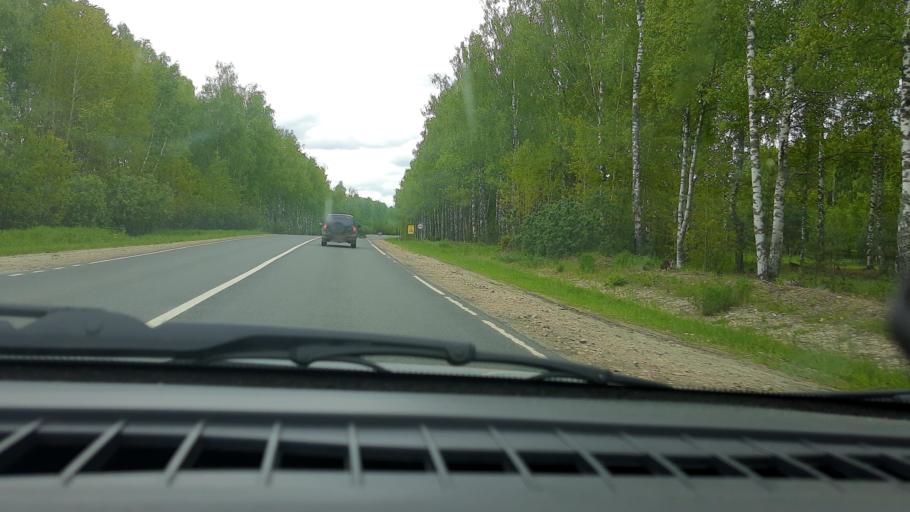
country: RU
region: Nizjnij Novgorod
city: Krasnyye Baki
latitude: 57.0776
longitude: 45.1441
